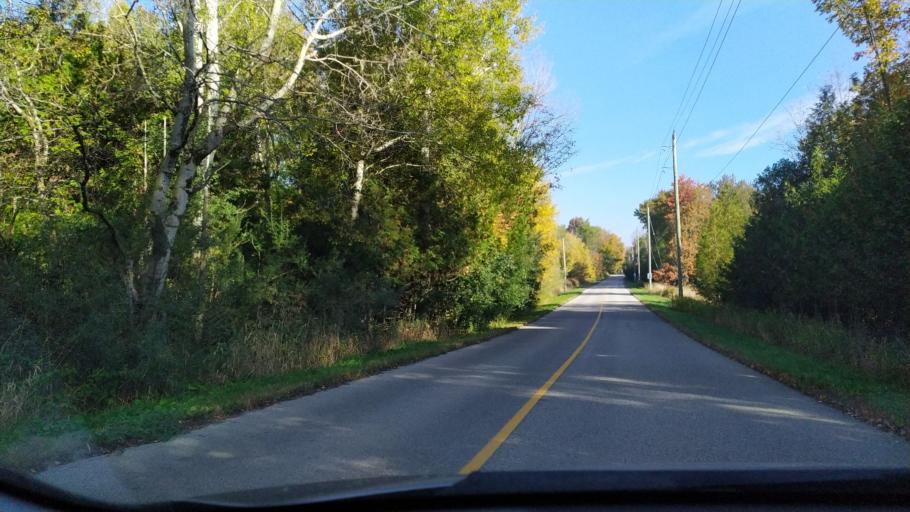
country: CA
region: Ontario
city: Waterloo
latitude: 43.4908
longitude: -80.6574
